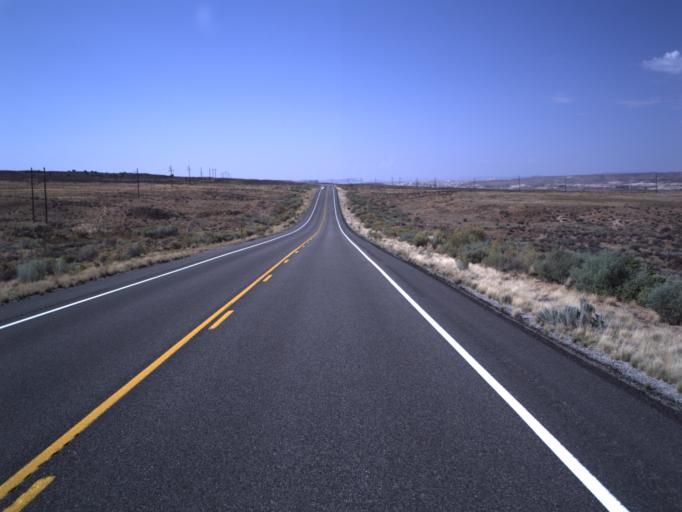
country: US
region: Utah
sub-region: San Juan County
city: Blanding
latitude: 37.3659
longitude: -109.5093
